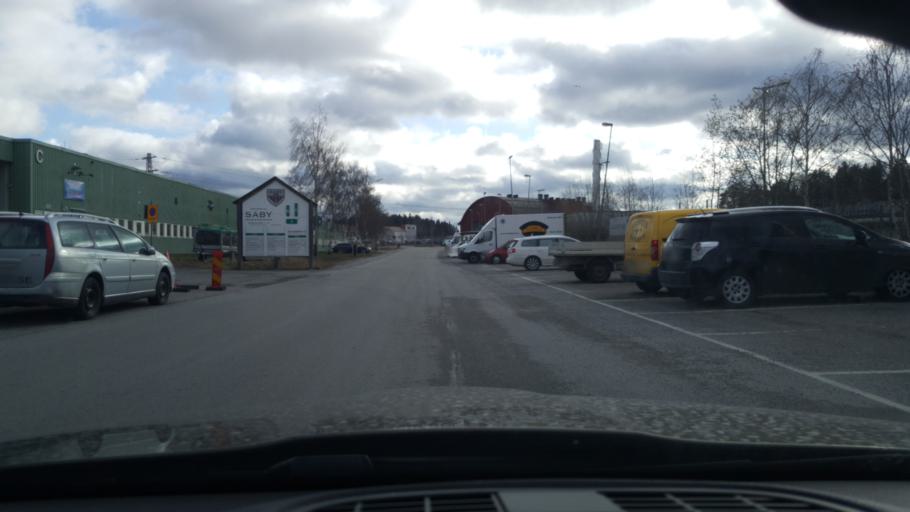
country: SE
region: Stockholm
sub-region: Osterakers Kommun
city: Akersberga
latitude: 59.4924
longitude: 18.2788
